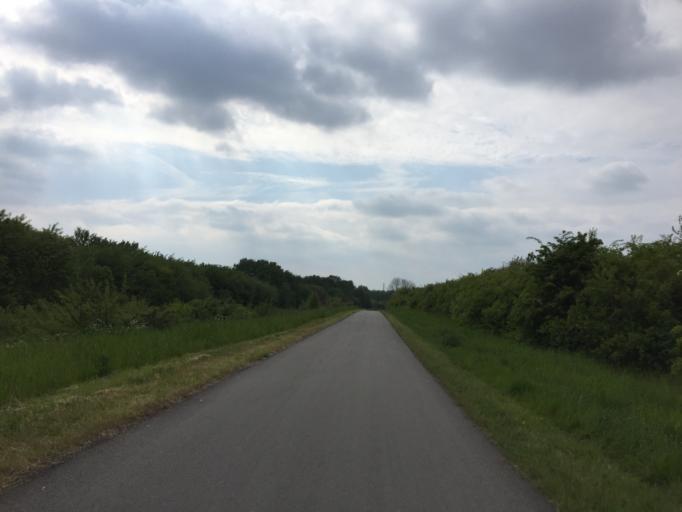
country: DK
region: Capital Region
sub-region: Hvidovre Kommune
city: Hvidovre
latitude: 55.6165
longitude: 12.4838
